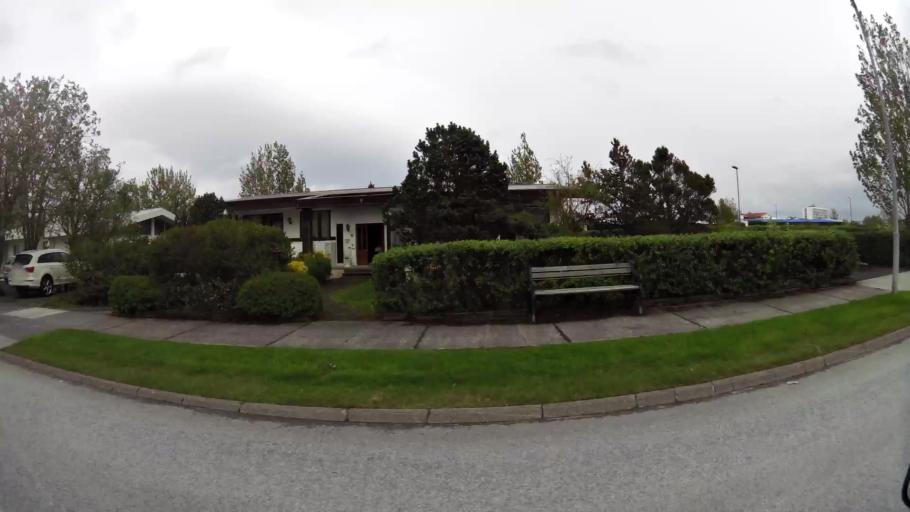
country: IS
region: Capital Region
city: Hafnarfjoerdur
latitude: 64.0781
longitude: -21.9677
